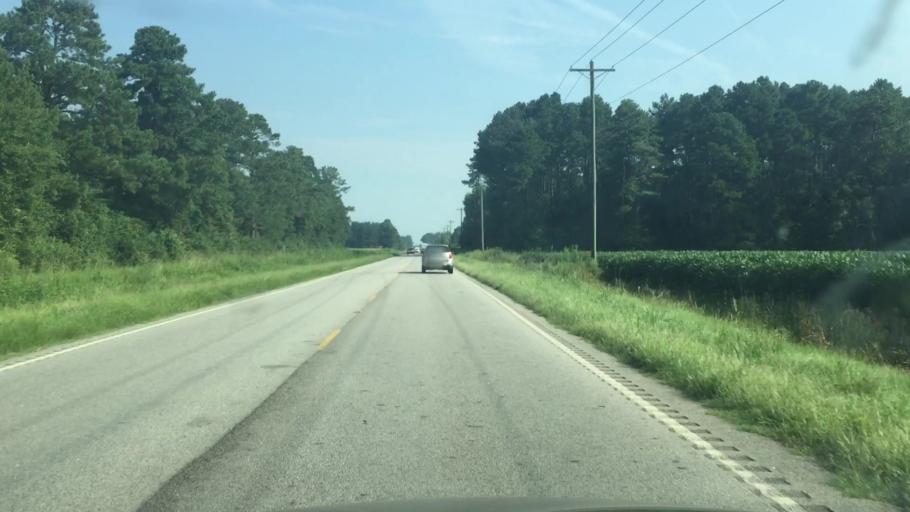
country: US
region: North Carolina
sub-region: Columbus County
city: Tabor City
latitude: 34.1226
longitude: -78.8758
